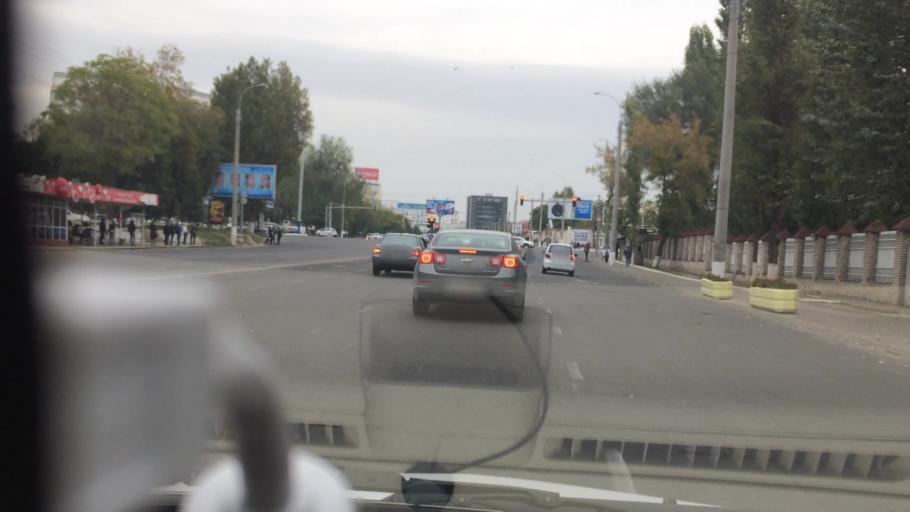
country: UZ
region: Toshkent
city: Salor
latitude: 41.3175
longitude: 69.3150
